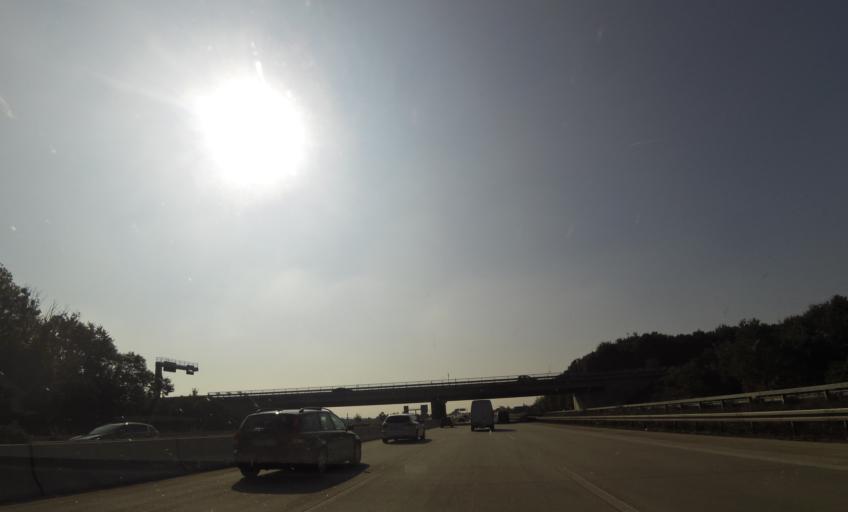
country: DE
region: Baden-Wuerttemberg
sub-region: Karlsruhe Region
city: Forst
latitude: 49.1490
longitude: 8.5604
